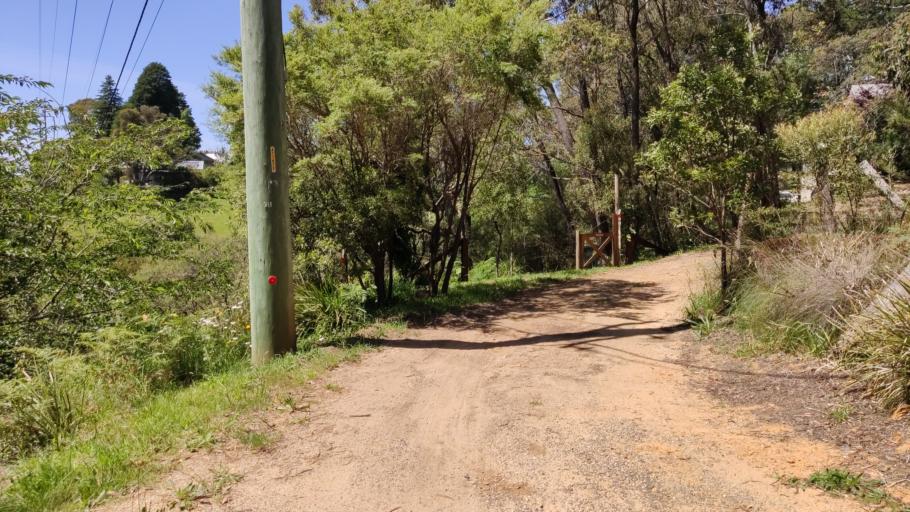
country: AU
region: New South Wales
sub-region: Blue Mountains Municipality
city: Blackheath
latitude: -33.6282
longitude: 150.2886
